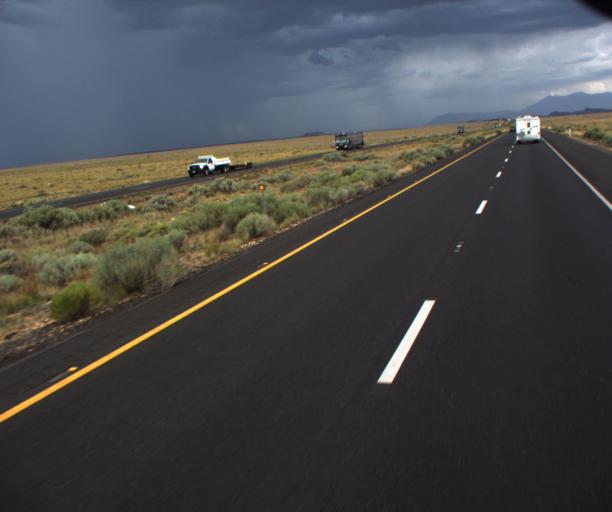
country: US
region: Arizona
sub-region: Coconino County
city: Flagstaff
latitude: 35.1478
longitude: -111.2343
